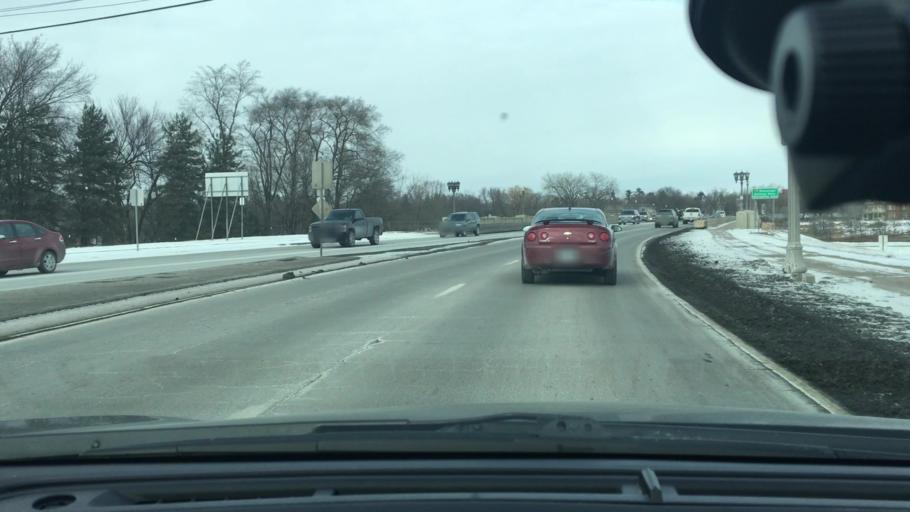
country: US
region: Minnesota
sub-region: Hennepin County
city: Champlin
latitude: 45.1900
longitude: -93.3965
